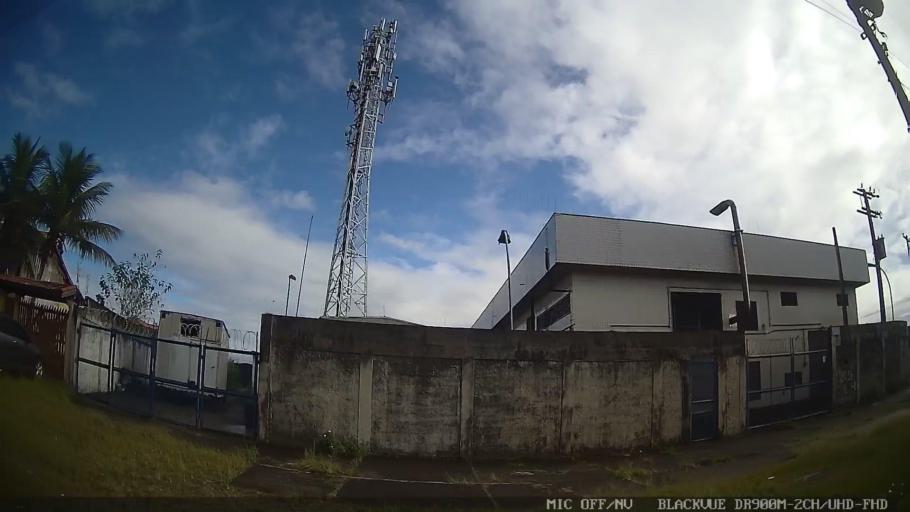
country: BR
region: Sao Paulo
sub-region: Itanhaem
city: Itanhaem
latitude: -24.2347
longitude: -46.8814
